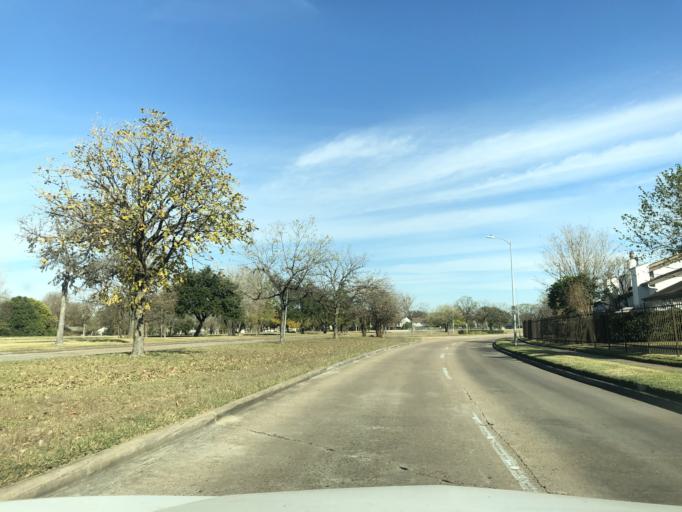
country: US
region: Texas
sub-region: Harris County
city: Bellaire
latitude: 29.6751
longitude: -95.5117
